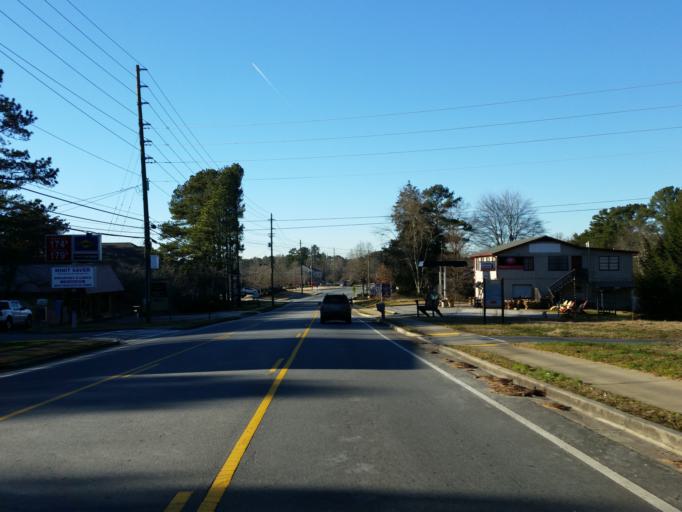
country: US
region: Georgia
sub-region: Cobb County
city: Kennesaw
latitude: 33.9659
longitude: -84.6634
